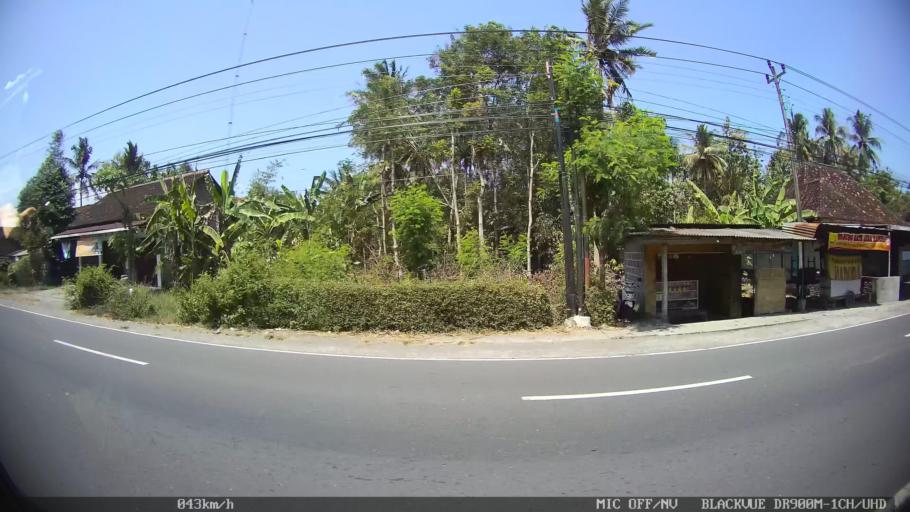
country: ID
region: Daerah Istimewa Yogyakarta
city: Srandakan
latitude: -7.9384
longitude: 110.2535
